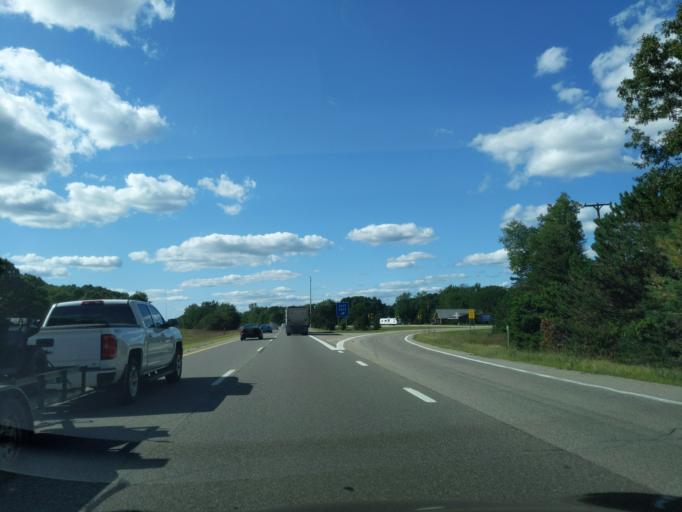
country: US
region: Michigan
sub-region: Muskegon County
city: Fruitport
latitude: 43.0911
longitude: -86.0968
